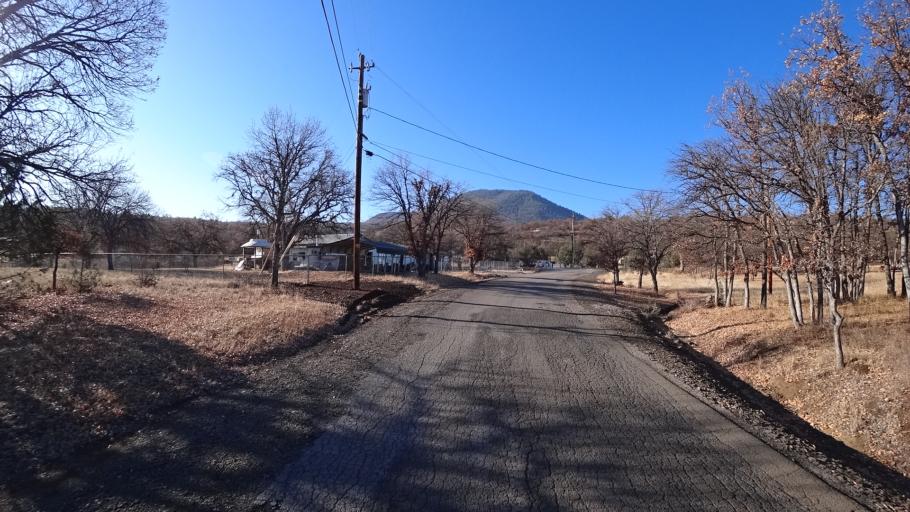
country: US
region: California
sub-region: Siskiyou County
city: Montague
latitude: 41.8881
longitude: -122.4916
